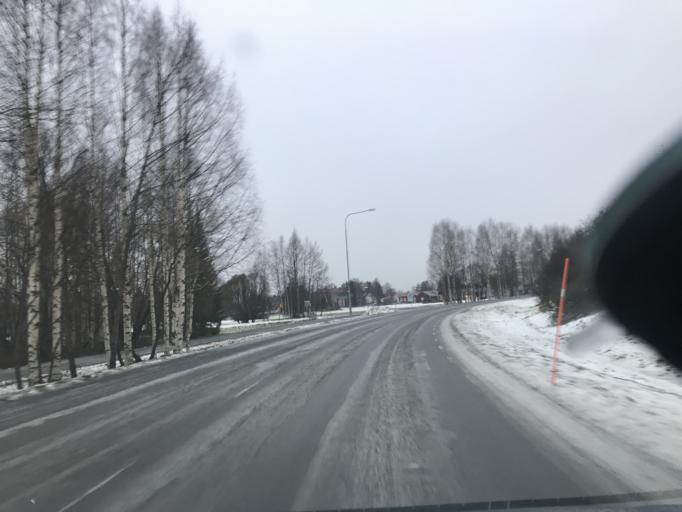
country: SE
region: Norrbotten
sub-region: Lulea Kommun
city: Sodra Sunderbyn
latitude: 65.6548
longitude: 21.9463
